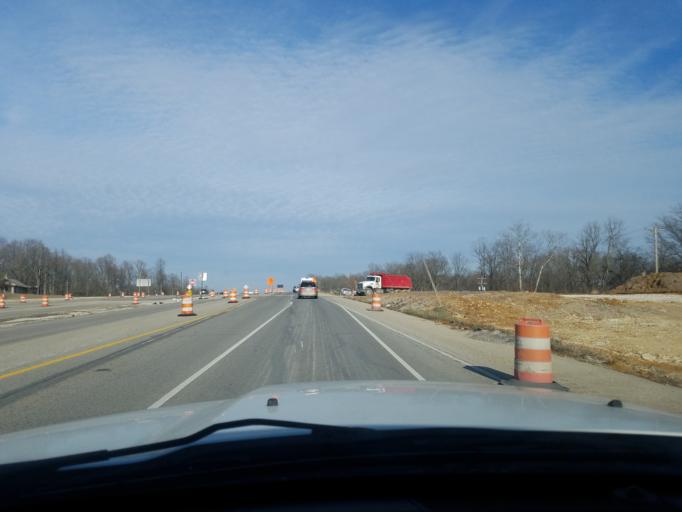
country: US
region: Indiana
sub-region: Monroe County
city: Bloomington
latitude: 39.2533
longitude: -86.5280
